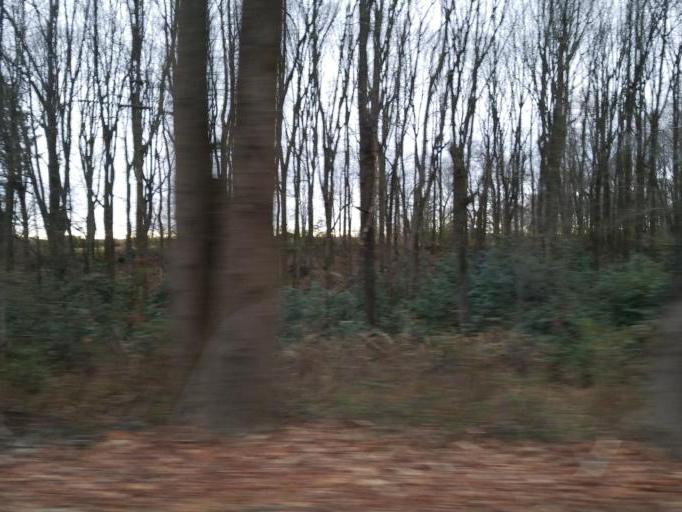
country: US
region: Georgia
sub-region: Dawson County
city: Dawsonville
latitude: 34.4942
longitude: -84.1876
